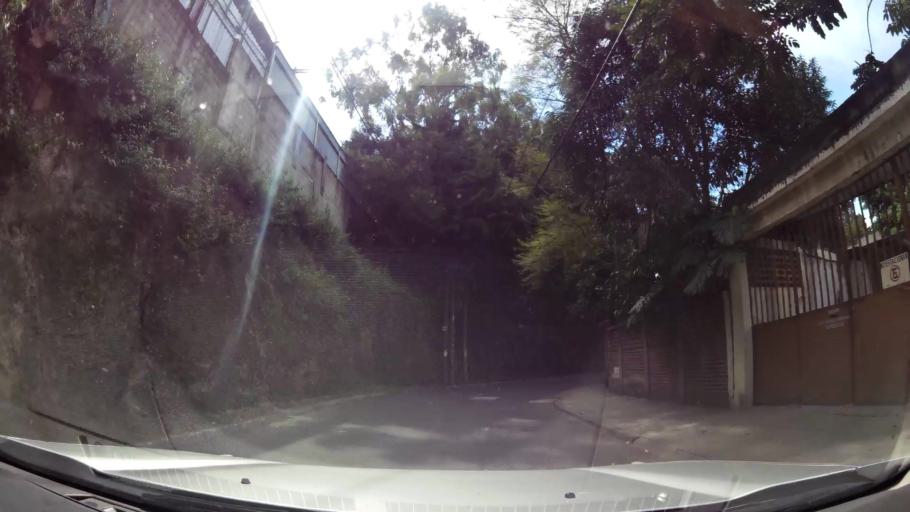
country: GT
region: Guatemala
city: Mixco
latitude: 14.6376
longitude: -90.5685
